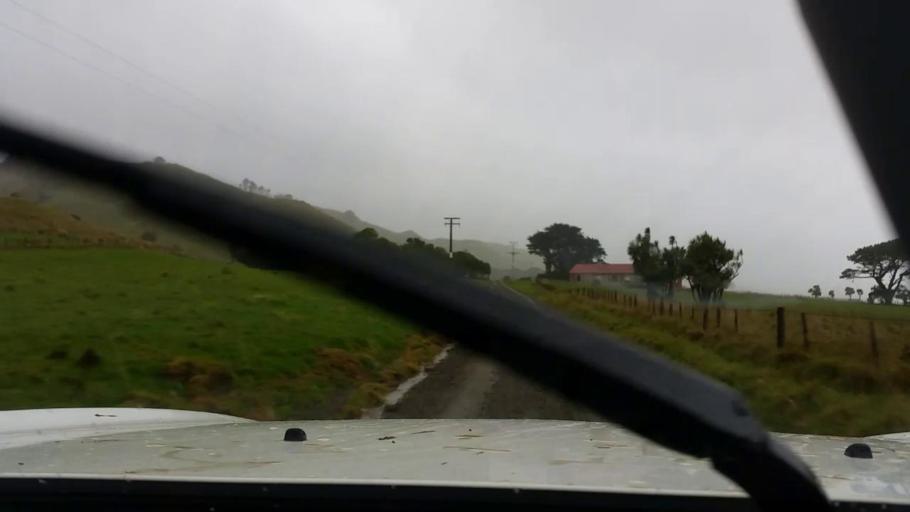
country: NZ
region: Wellington
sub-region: Masterton District
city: Masterton
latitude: -41.2634
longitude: 175.8935
